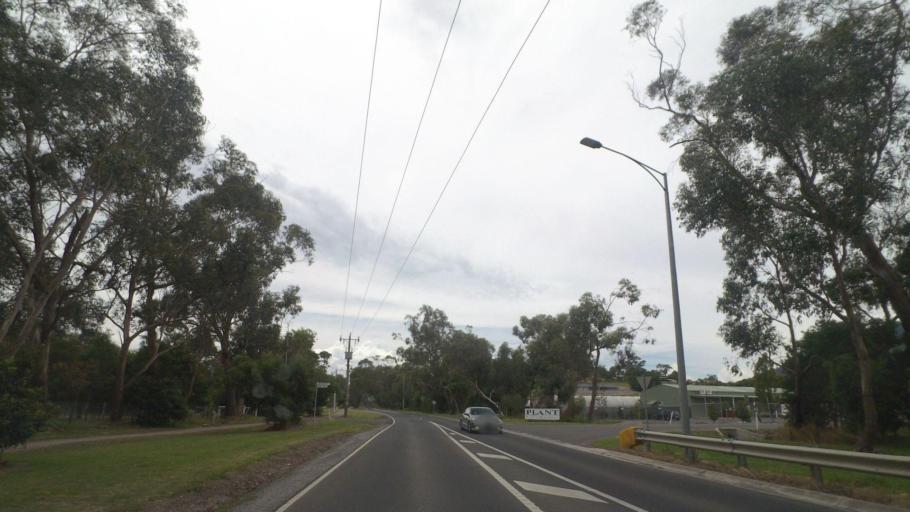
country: AU
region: Victoria
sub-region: Knox
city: The Basin
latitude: -37.8407
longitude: 145.3187
